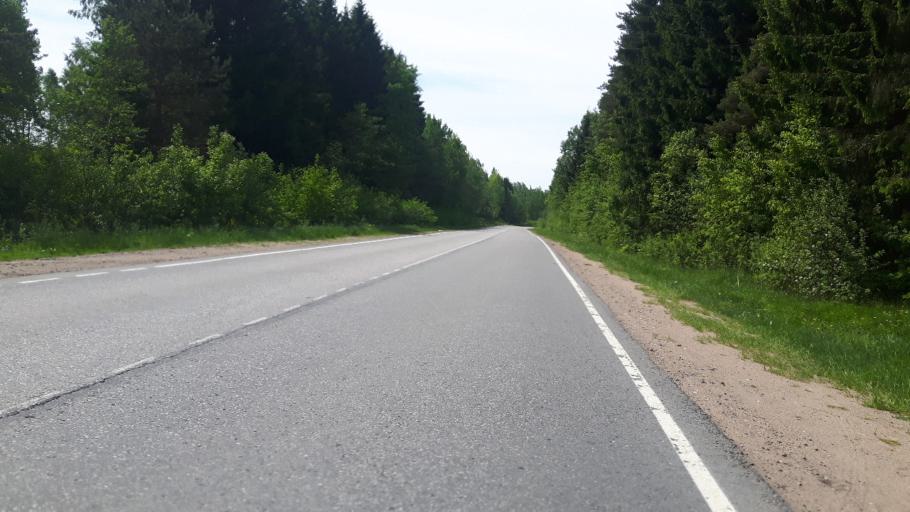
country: RU
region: Leningrad
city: Ust'-Luga
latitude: 59.6480
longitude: 28.2275
